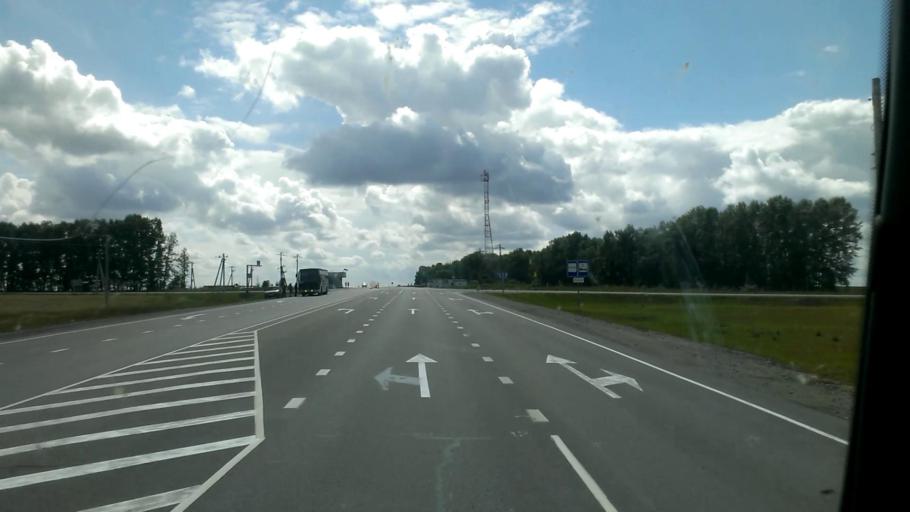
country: RU
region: Altai Krai
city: Troitskoye
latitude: 52.9682
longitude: 84.7501
